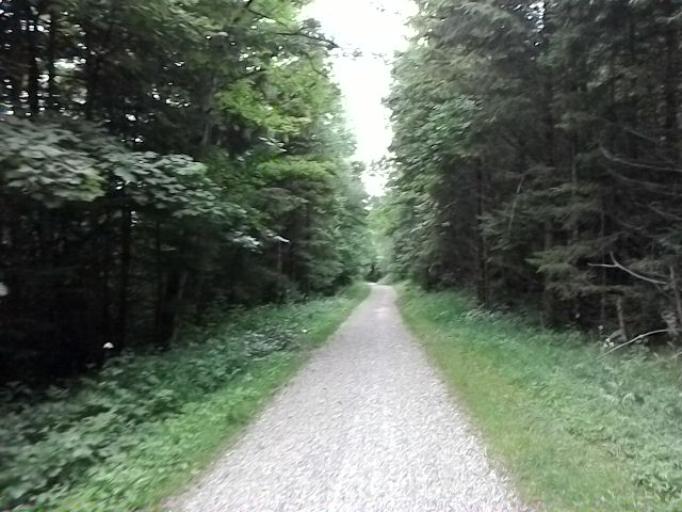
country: DE
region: Bavaria
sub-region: Upper Bavaria
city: Mittenwald
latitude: 47.4666
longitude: 11.2826
